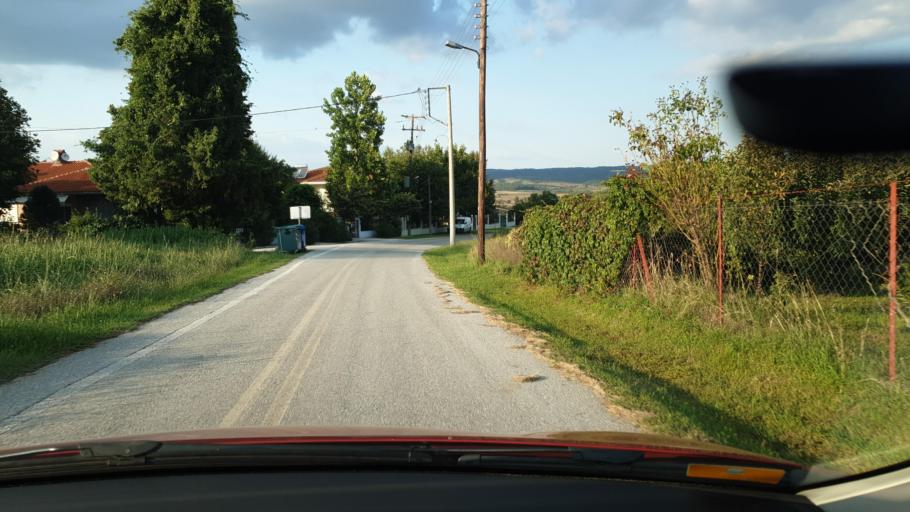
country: GR
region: Central Macedonia
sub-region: Nomos Thessalonikis
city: Gerakarou
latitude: 40.5641
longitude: 23.2823
